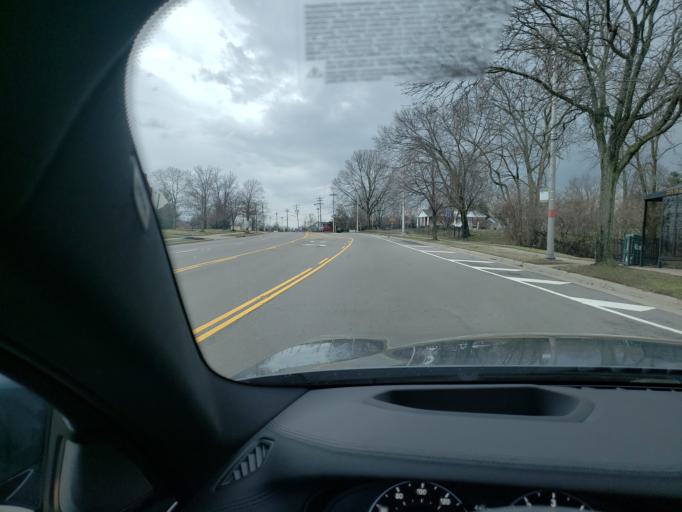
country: US
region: Ohio
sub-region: Hamilton County
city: Springdale
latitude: 39.2817
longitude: -84.4853
